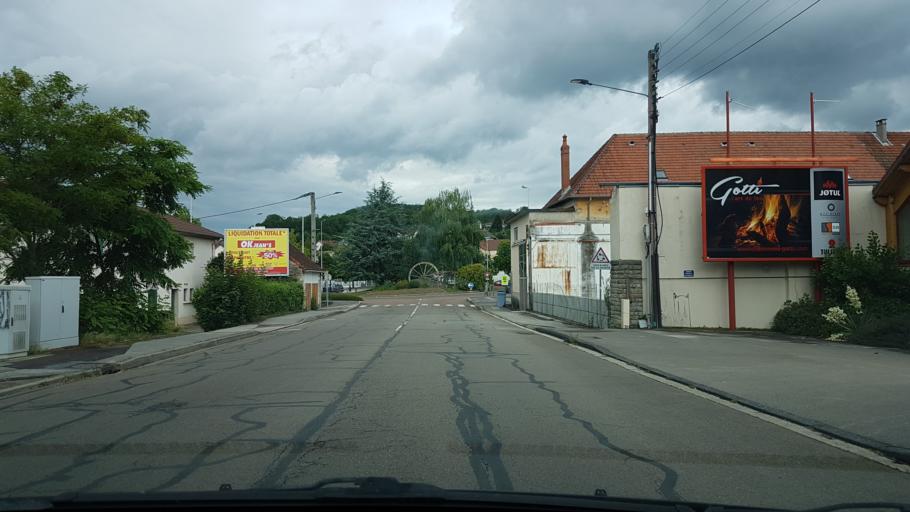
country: FR
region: Franche-Comte
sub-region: Departement du Jura
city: Lons-le-Saunier
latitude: 46.6747
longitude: 5.5431
